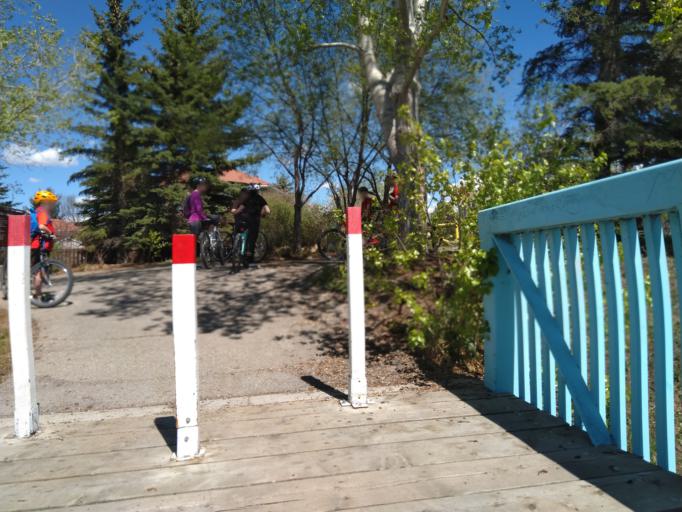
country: CA
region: Alberta
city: Chestermere
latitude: 51.0201
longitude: -113.8283
